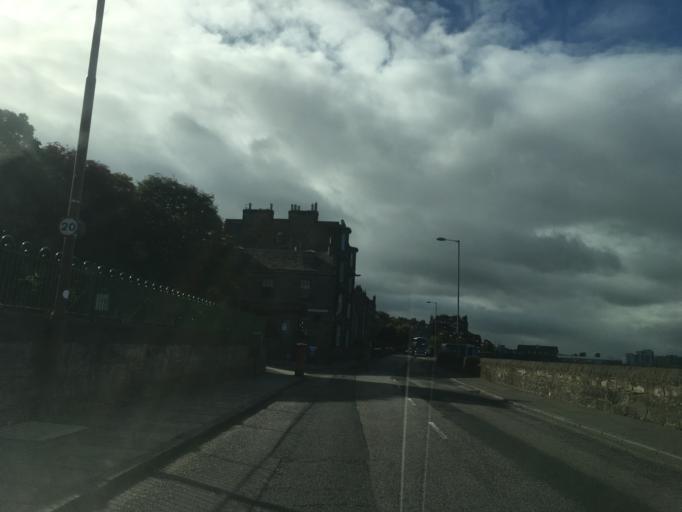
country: GB
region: Scotland
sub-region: Edinburgh
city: Edinburgh
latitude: 55.9800
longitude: -3.2011
